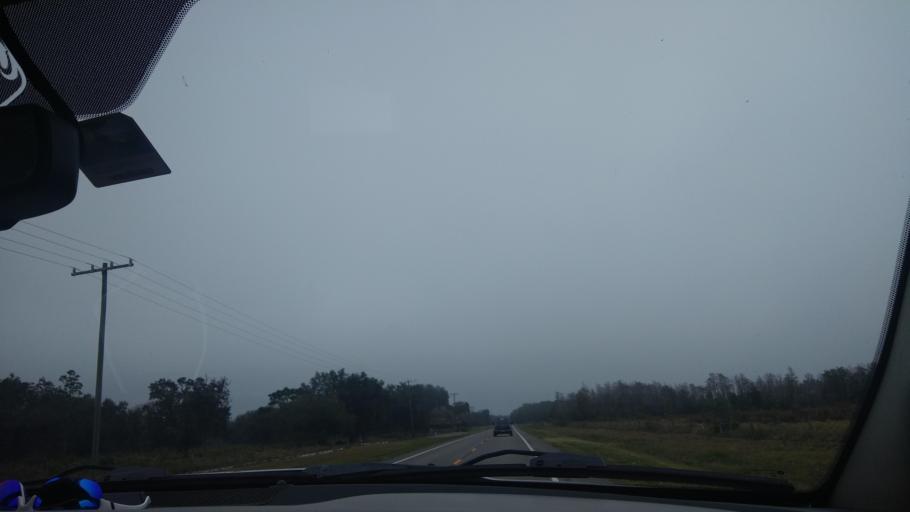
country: US
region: Florida
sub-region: Brevard County
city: June Park
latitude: 27.9317
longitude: -80.9960
